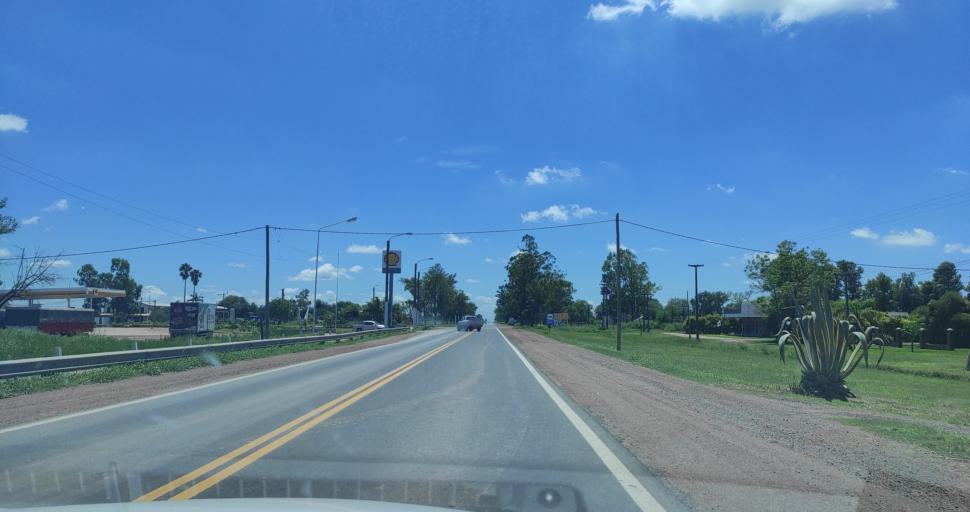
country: AR
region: Chaco
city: Las Brenas
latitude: -27.1005
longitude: -61.0674
